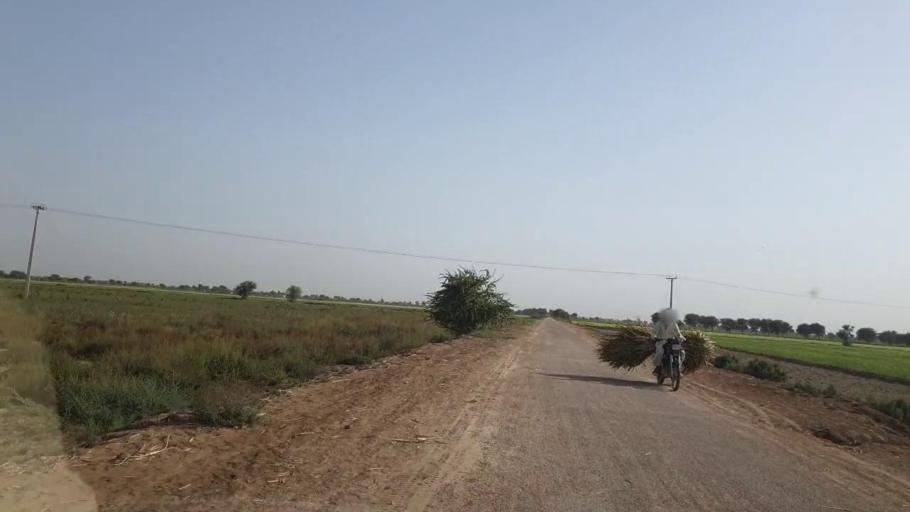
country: PK
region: Sindh
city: Tando Ghulam Ali
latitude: 25.0939
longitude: 68.8529
